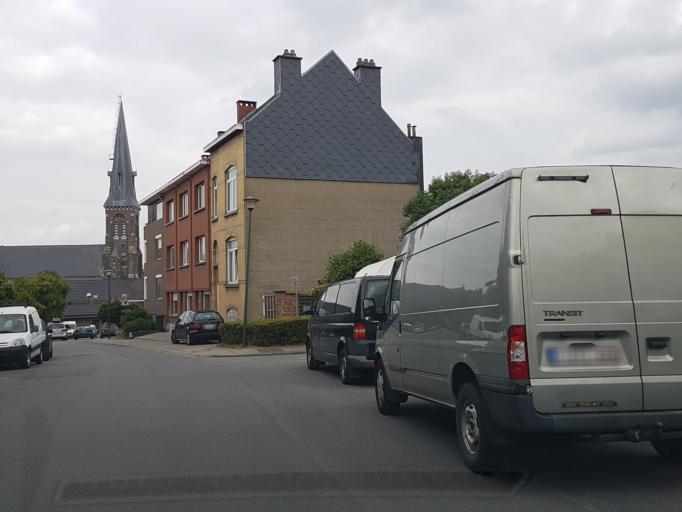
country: BE
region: Flanders
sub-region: Provincie Vlaams-Brabant
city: Kraainem
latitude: 50.8700
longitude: 4.4483
